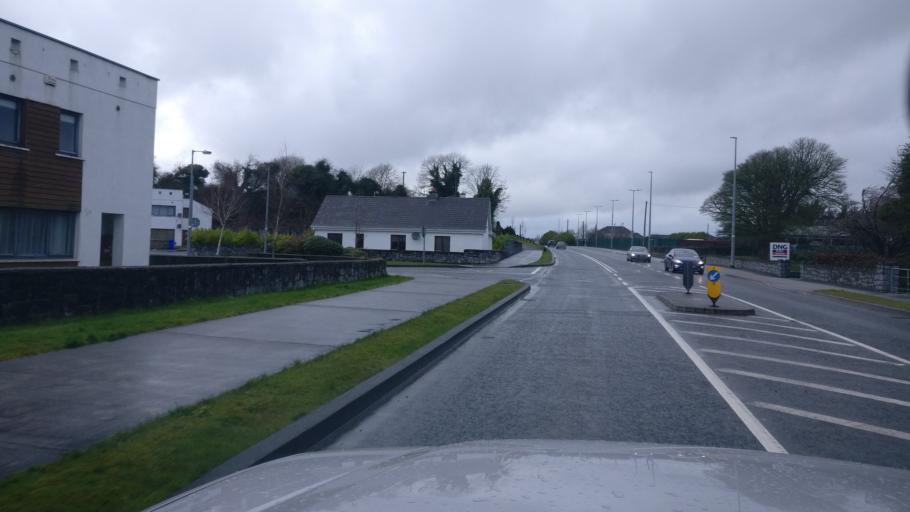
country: IE
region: Leinster
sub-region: An Iarmhi
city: Athlone
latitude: 53.4243
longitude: -7.9996
